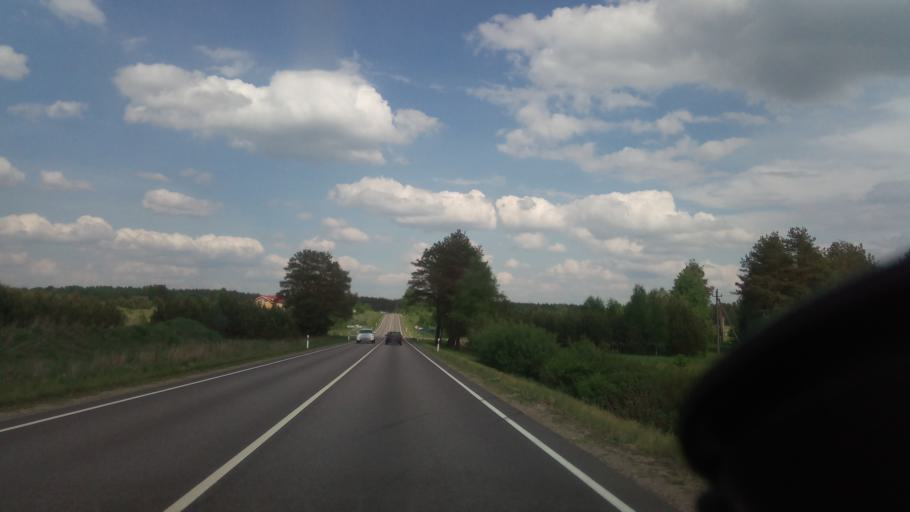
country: LT
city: Trakai
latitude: 54.6121
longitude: 24.8876
